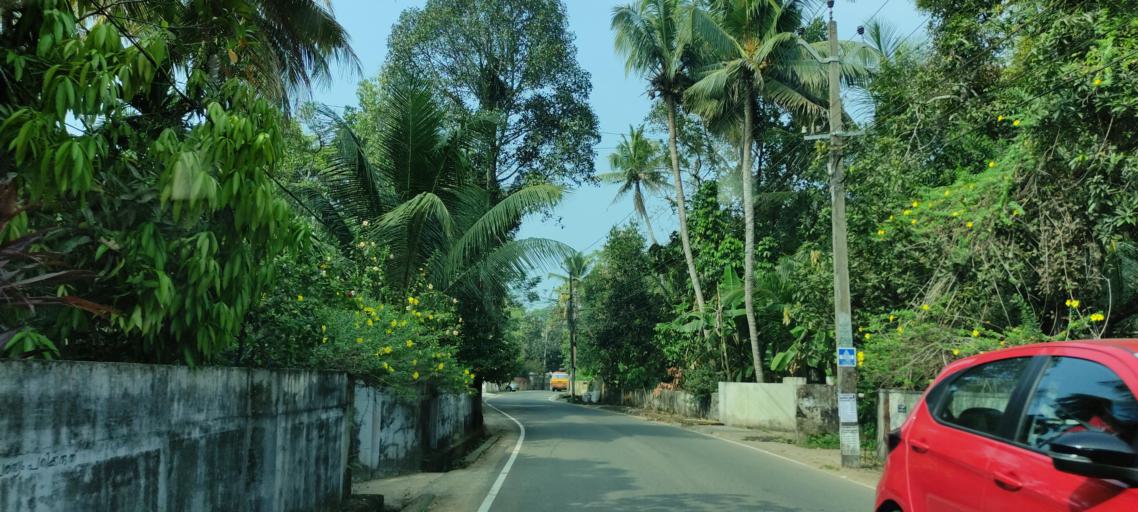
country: IN
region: Kerala
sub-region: Kottayam
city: Vaikam
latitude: 9.7563
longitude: 76.4021
